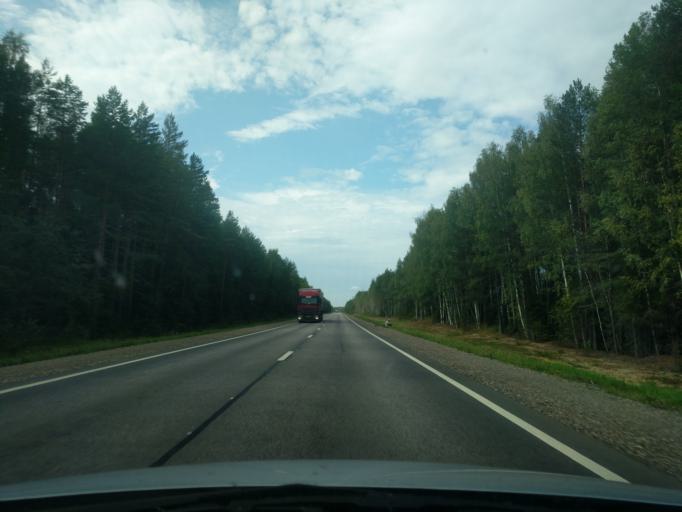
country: RU
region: Kostroma
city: Kadyy
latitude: 57.7967
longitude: 42.9062
